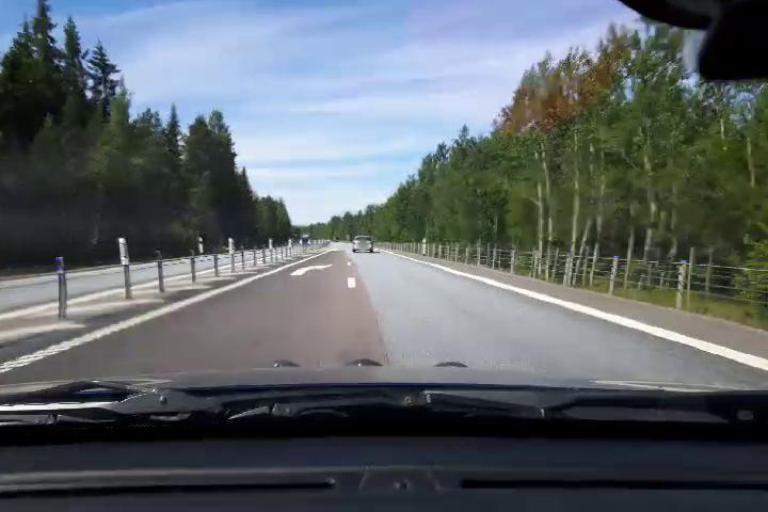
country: SE
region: Gaevleborg
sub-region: Gavle Kommun
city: Norrsundet
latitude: 60.9182
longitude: 17.0136
